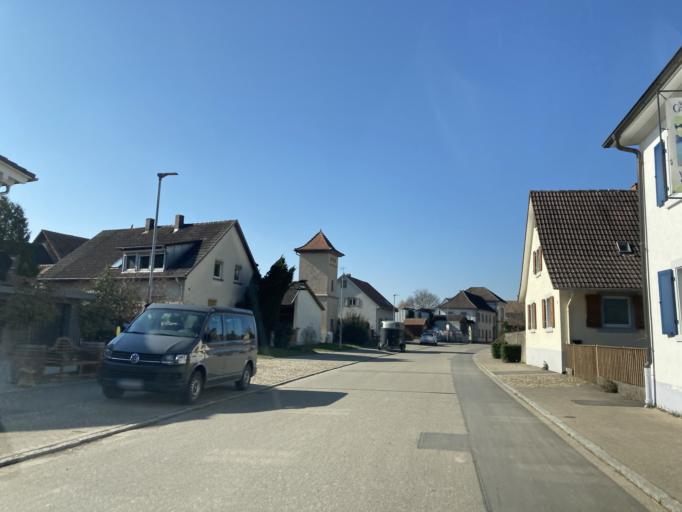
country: DE
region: Baden-Wuerttemberg
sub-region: Freiburg Region
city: Buggingen
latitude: 47.8586
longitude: 7.6416
